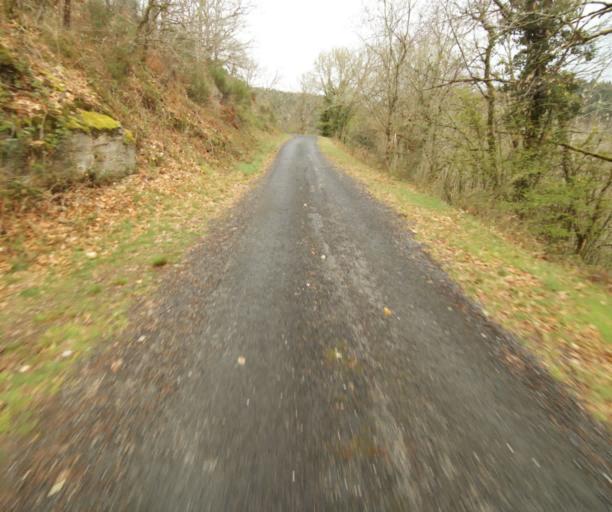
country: FR
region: Limousin
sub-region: Departement de la Correze
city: Saint-Privat
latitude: 45.2064
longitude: 2.0315
